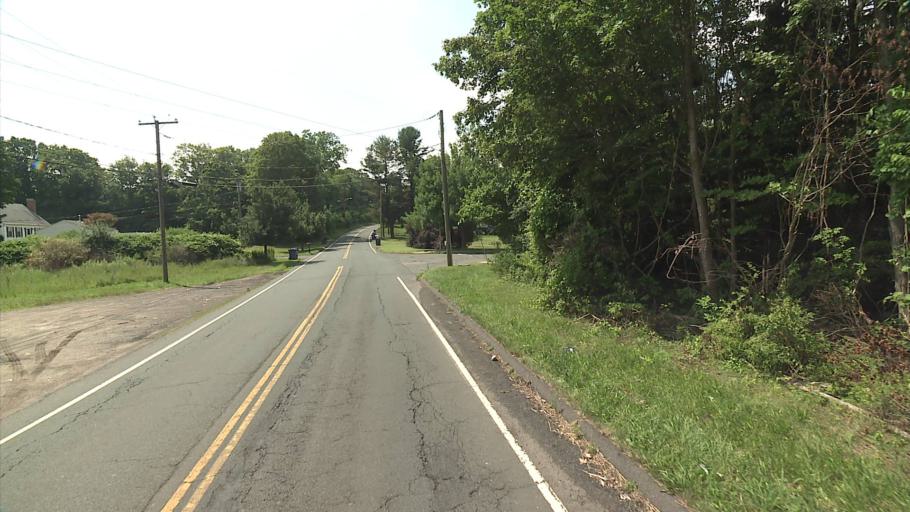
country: US
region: Connecticut
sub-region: Middlesex County
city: Middletown
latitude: 41.5755
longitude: -72.7019
